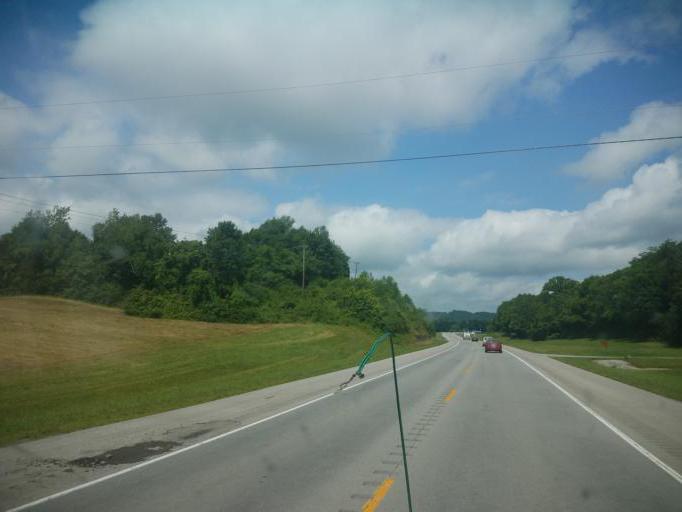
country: US
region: Kentucky
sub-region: Cumberland County
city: Burkesville
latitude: 36.7681
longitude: -85.3525
